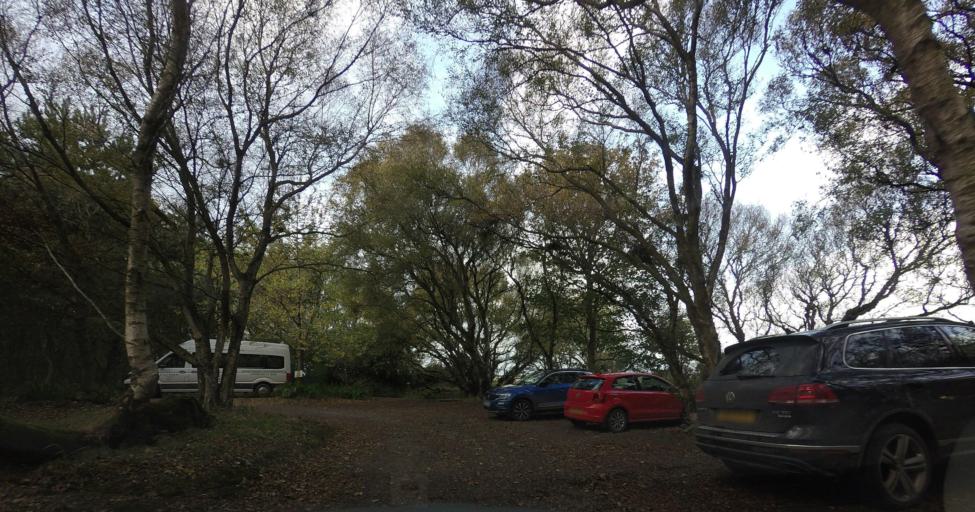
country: GB
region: Scotland
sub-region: Aberdeenshire
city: Whitehills
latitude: 57.6629
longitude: -2.6050
